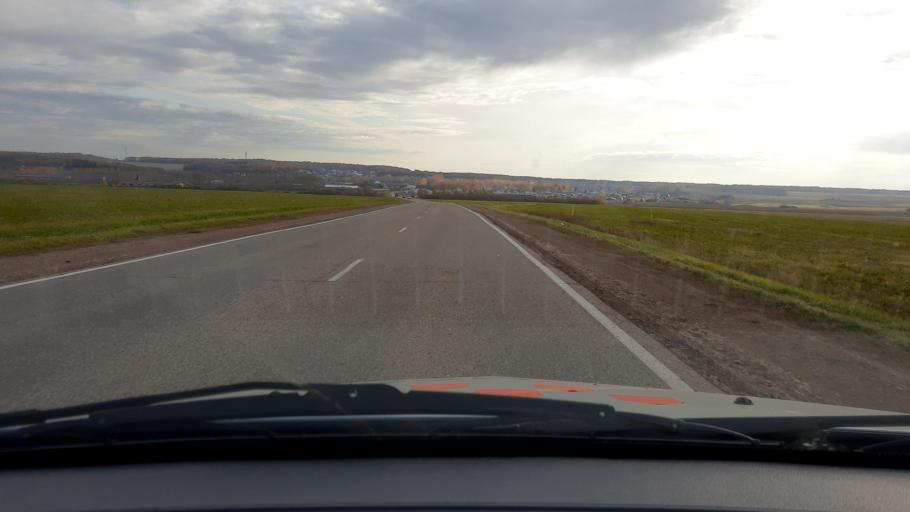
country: RU
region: Bashkortostan
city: Avdon
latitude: 54.8219
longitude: 55.6660
